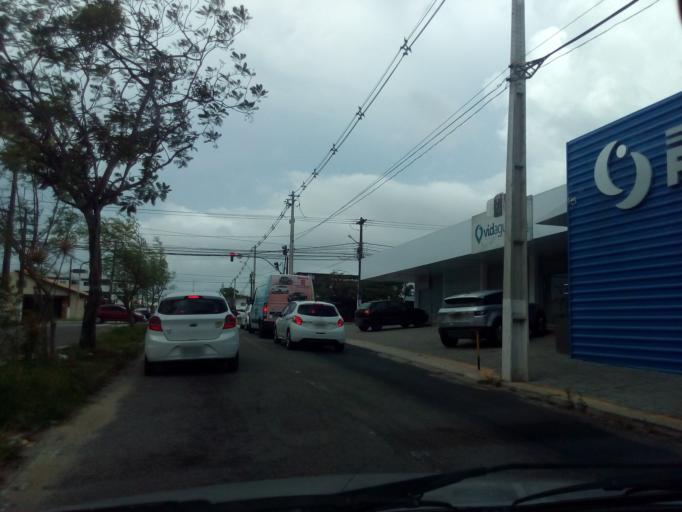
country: BR
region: Rio Grande do Norte
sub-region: Natal
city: Natal
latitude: -5.8140
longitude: -35.2131
